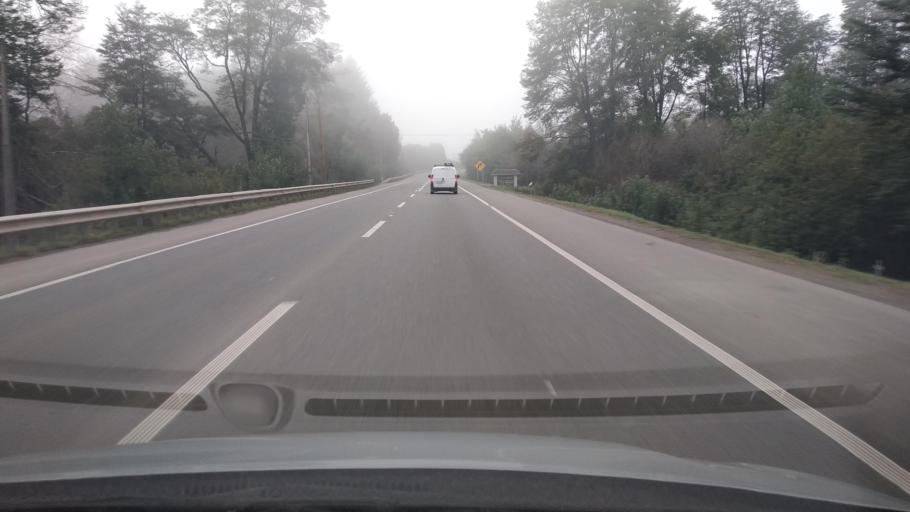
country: CL
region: Los Lagos
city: Las Animas
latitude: -39.7532
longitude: -73.2289
